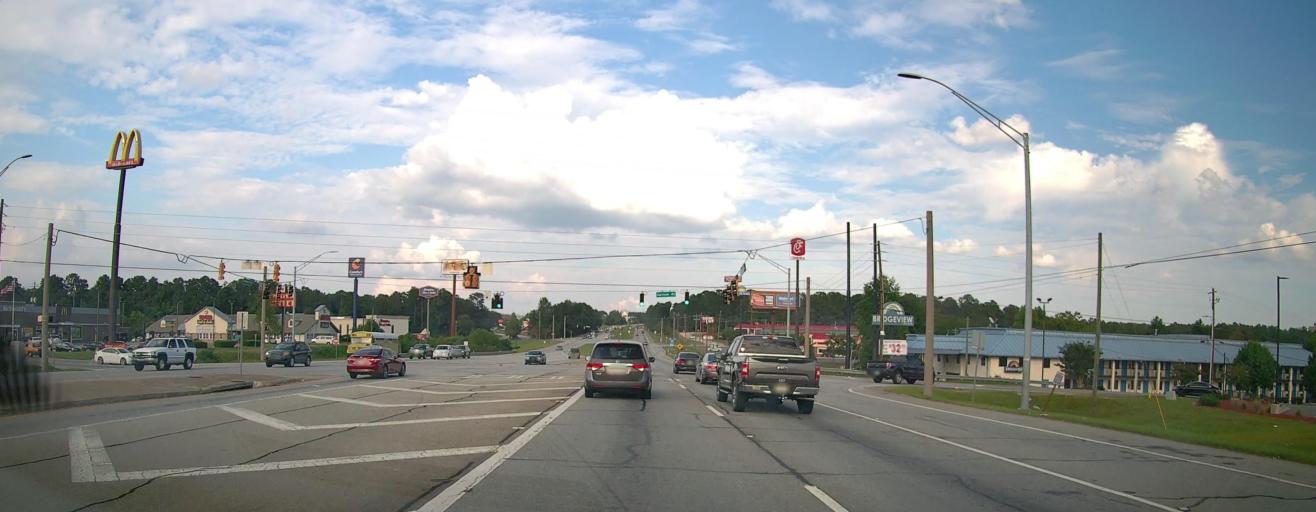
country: US
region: Georgia
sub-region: Bibb County
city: West Point
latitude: 32.8107
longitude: -83.7229
